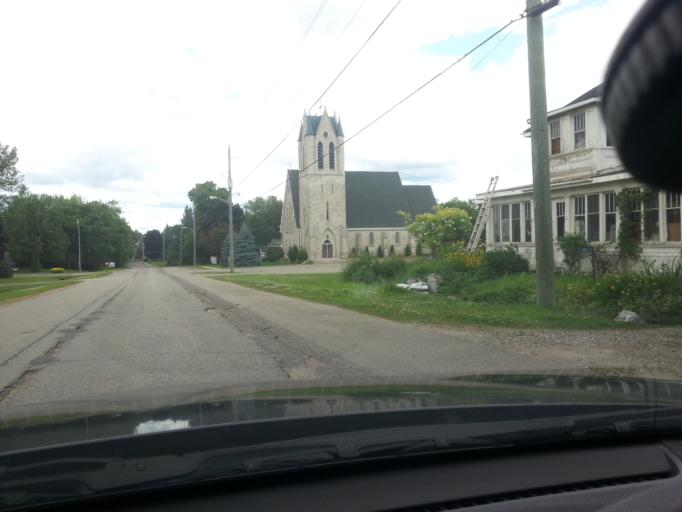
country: CA
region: Ontario
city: Gananoque
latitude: 44.6046
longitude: -76.2185
